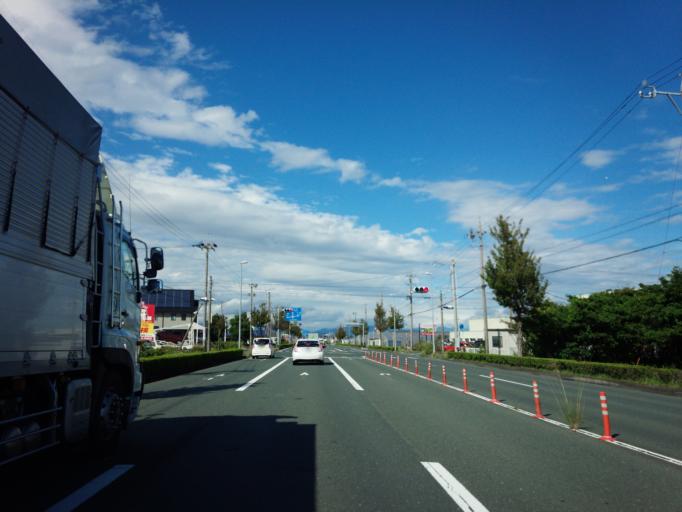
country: JP
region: Shizuoka
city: Hamakita
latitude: 34.7537
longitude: 137.7922
